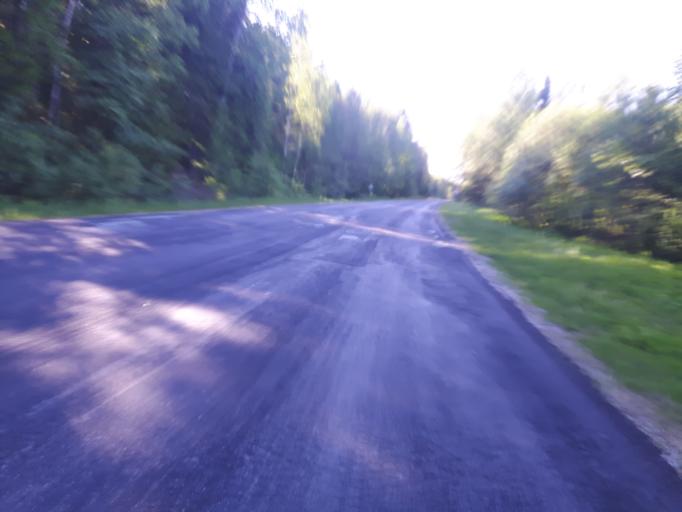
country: EE
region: Harju
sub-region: Loksa linn
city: Loksa
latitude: 59.5617
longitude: 25.9819
